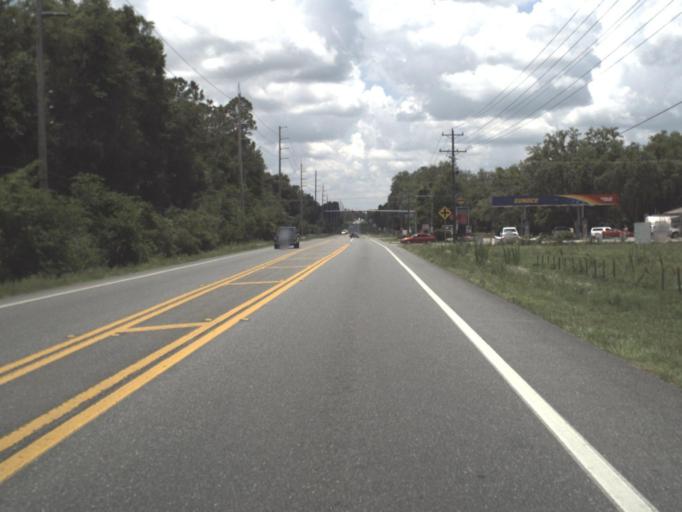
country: US
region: Florida
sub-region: Alachua County
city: Newberry
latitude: 29.6353
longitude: -82.6881
